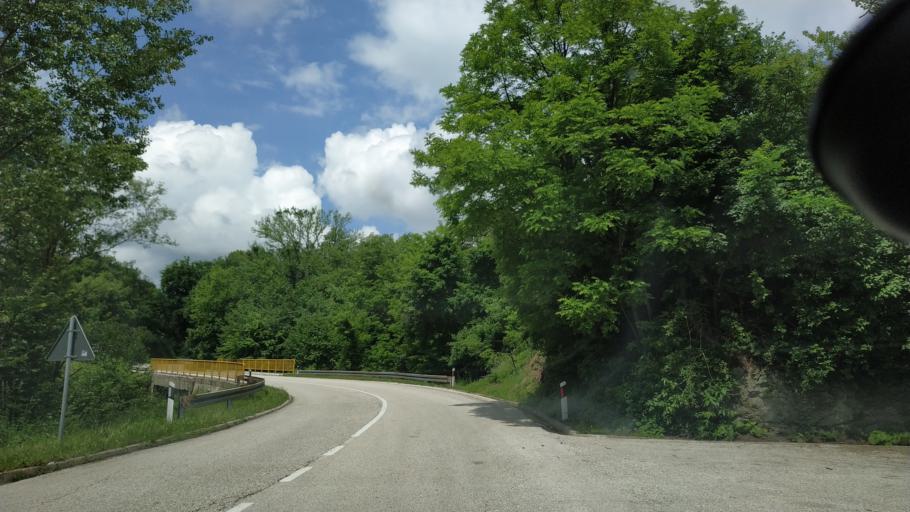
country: RS
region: Central Serbia
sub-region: Borski Okrug
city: Bor
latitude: 44.0607
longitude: 22.0447
